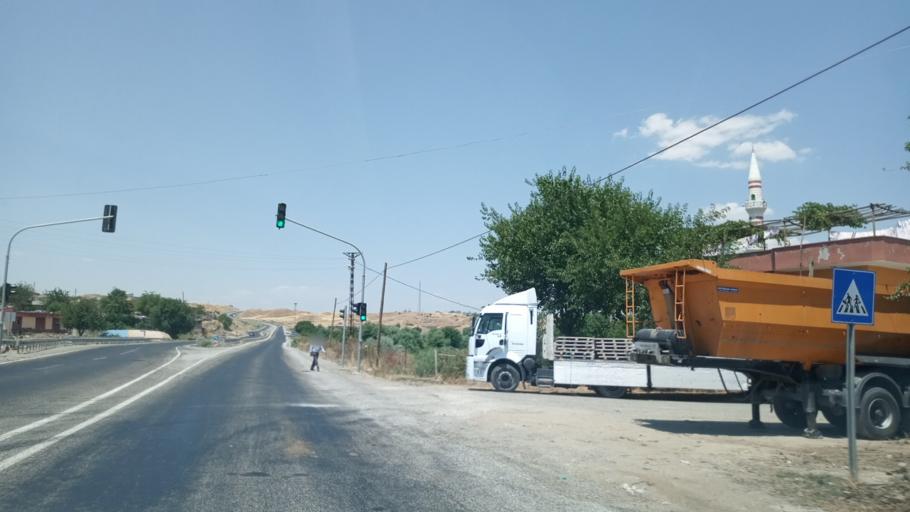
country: TR
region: Batman
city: Kozluk
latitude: 38.1488
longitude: 41.3933
